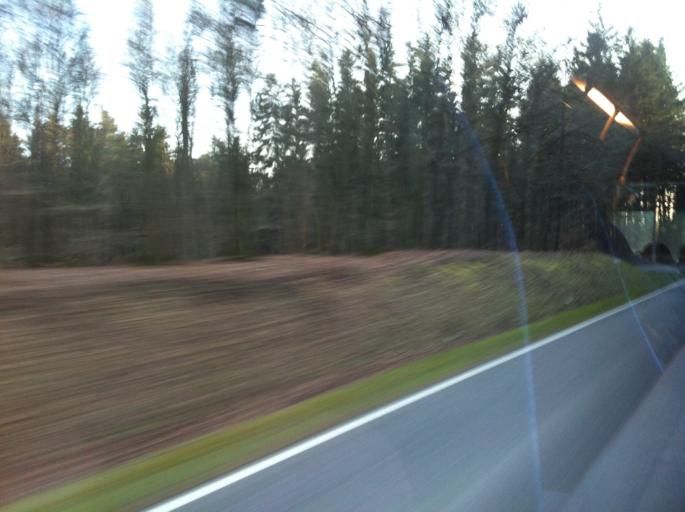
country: DE
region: Baden-Wuerttemberg
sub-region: Karlsruhe Region
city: Fahrenbach
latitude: 49.4598
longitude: 9.1124
